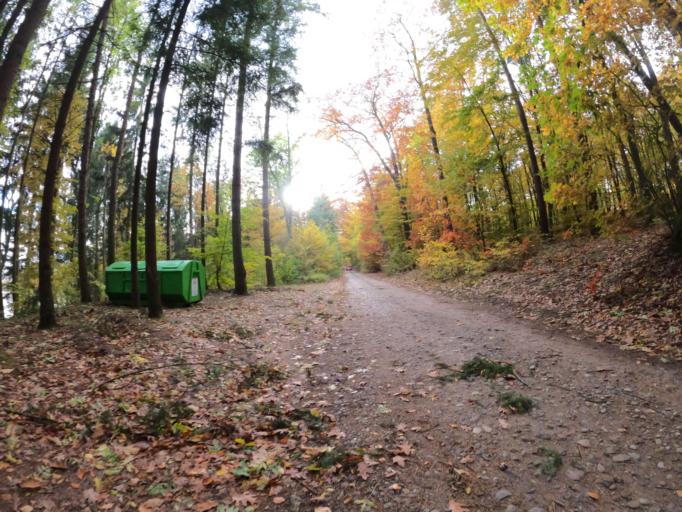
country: PL
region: West Pomeranian Voivodeship
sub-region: Powiat mysliborski
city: Barlinek
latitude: 52.9074
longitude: 15.2735
